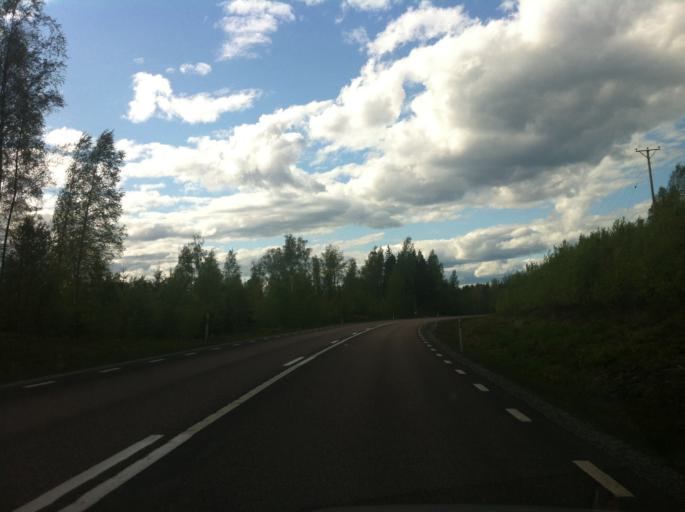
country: SE
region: Vaermland
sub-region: Filipstads Kommun
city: Filipstad
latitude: 59.6794
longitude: 14.2071
